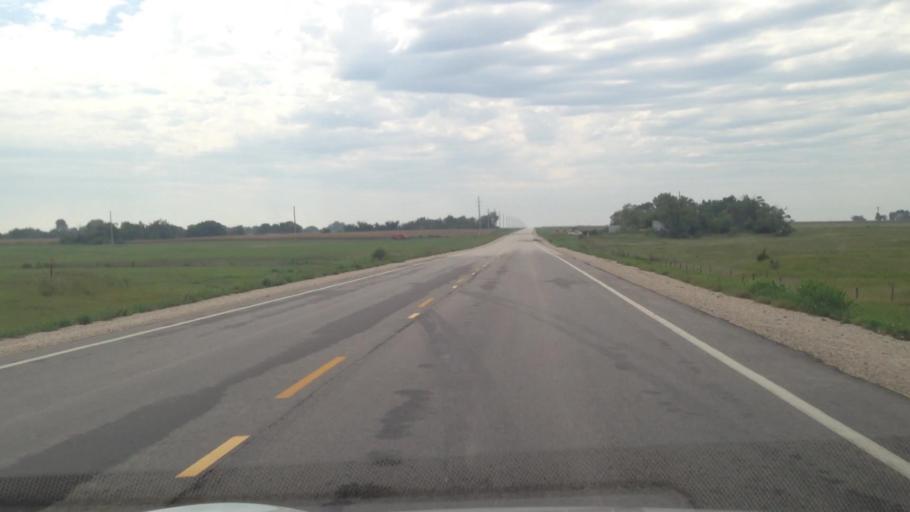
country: US
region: Kansas
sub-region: Anderson County
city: Garnett
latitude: 38.0708
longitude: -95.1694
